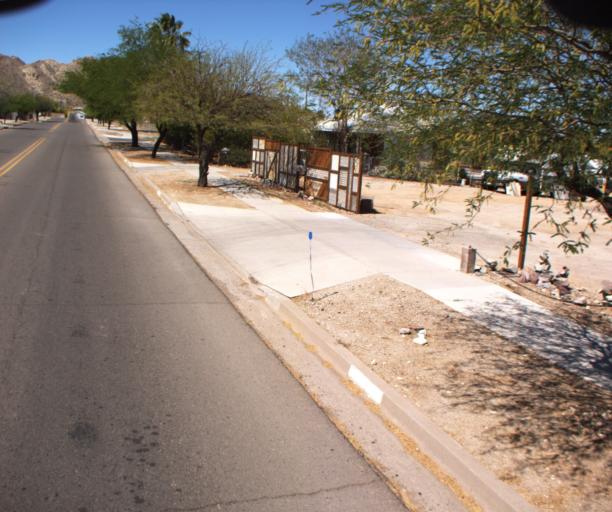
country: US
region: Arizona
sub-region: Pima County
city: Ajo
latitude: 32.3748
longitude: -112.8684
